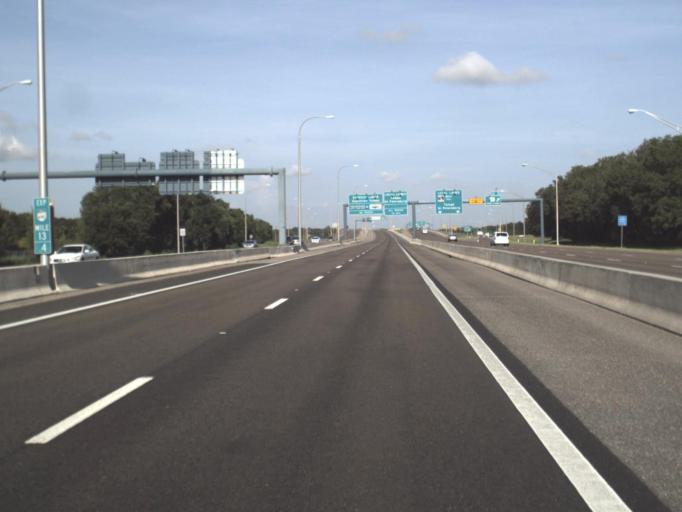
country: US
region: Florida
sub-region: Hillsborough County
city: Progress Village
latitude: 27.9295
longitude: -82.3441
